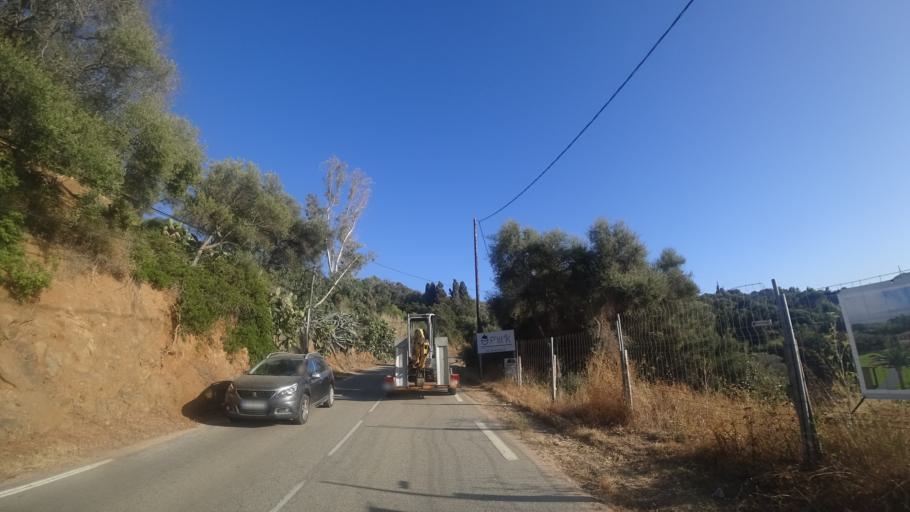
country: FR
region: Corsica
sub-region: Departement de la Corse-du-Sud
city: Cargese
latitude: 42.1413
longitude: 8.6016
